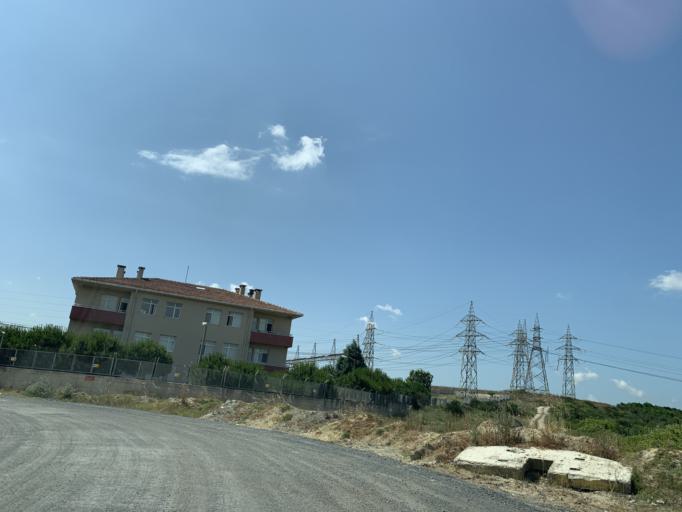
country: TR
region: Istanbul
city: Esenyurt
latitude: 41.0878
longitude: 28.6926
